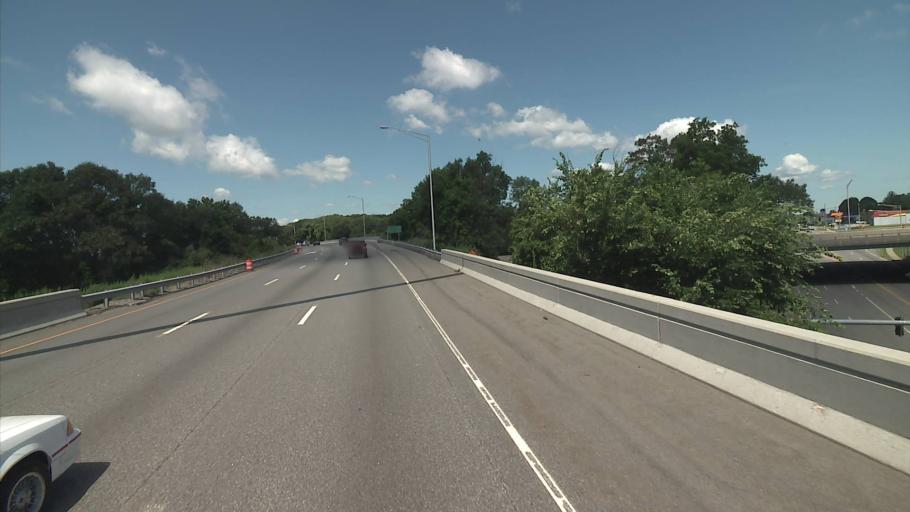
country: US
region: Connecticut
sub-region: New London County
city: Groton
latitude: 41.3650
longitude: -72.0682
